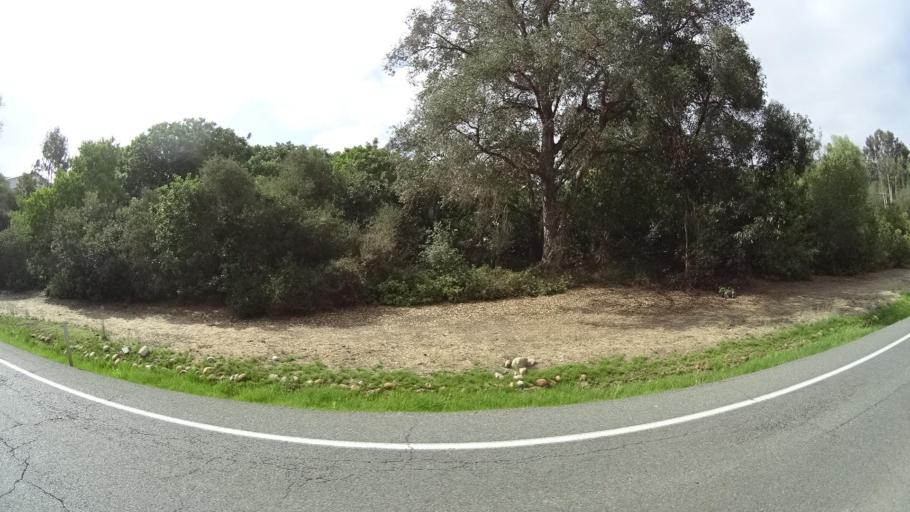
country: US
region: California
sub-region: San Diego County
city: Rancho Santa Fe
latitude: 33.0219
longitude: -117.2085
